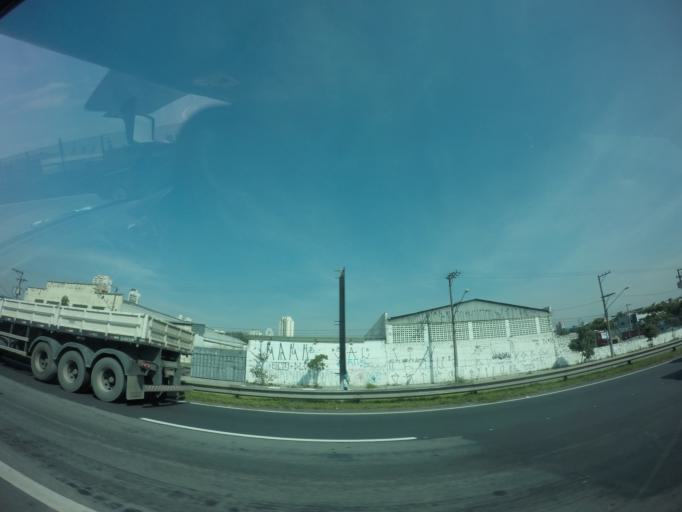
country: BR
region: Sao Paulo
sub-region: Guarulhos
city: Guarulhos
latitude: -23.5125
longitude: -46.5763
